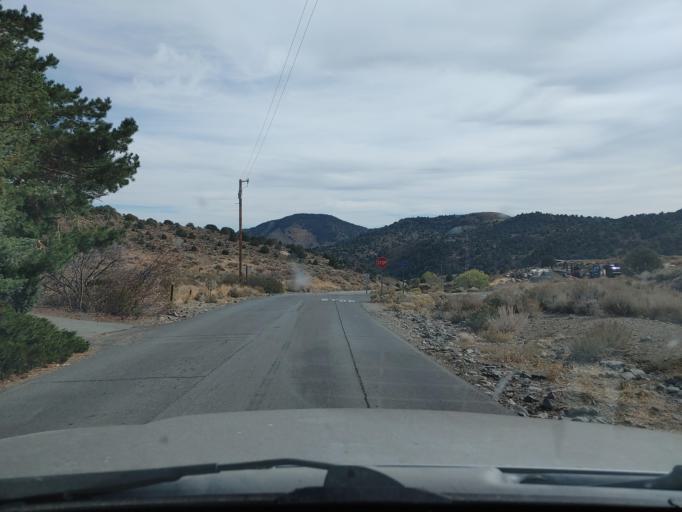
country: US
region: Nevada
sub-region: Storey County
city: Virginia City
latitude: 39.3110
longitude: -119.6410
